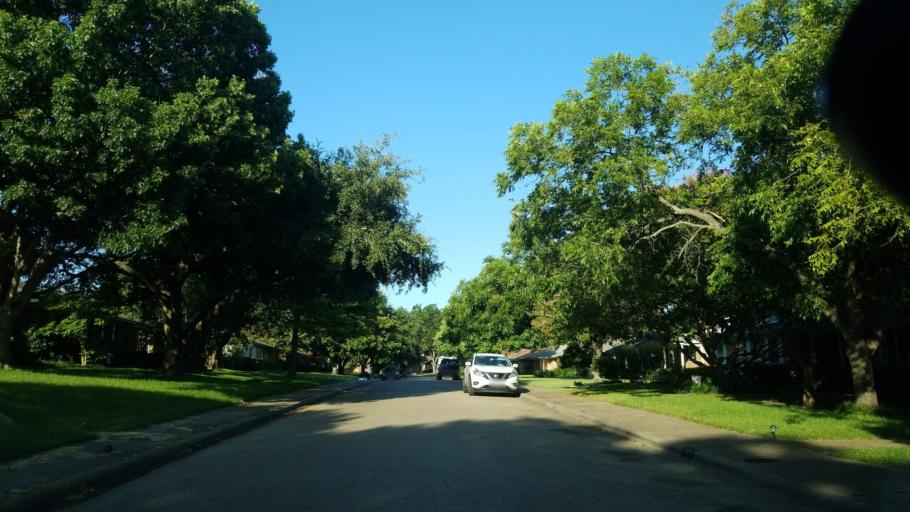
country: US
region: Texas
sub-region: Dallas County
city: Highland Park
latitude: 32.7830
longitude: -96.7097
